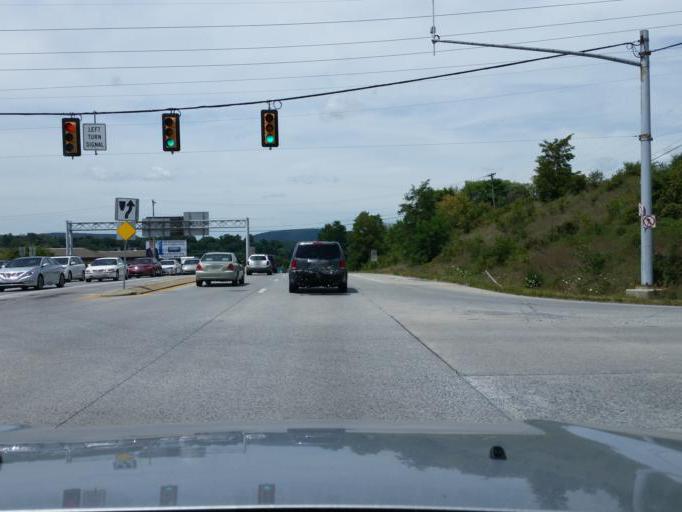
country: US
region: Pennsylvania
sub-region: Blair County
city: Lakemont
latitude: 40.4804
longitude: -78.3966
